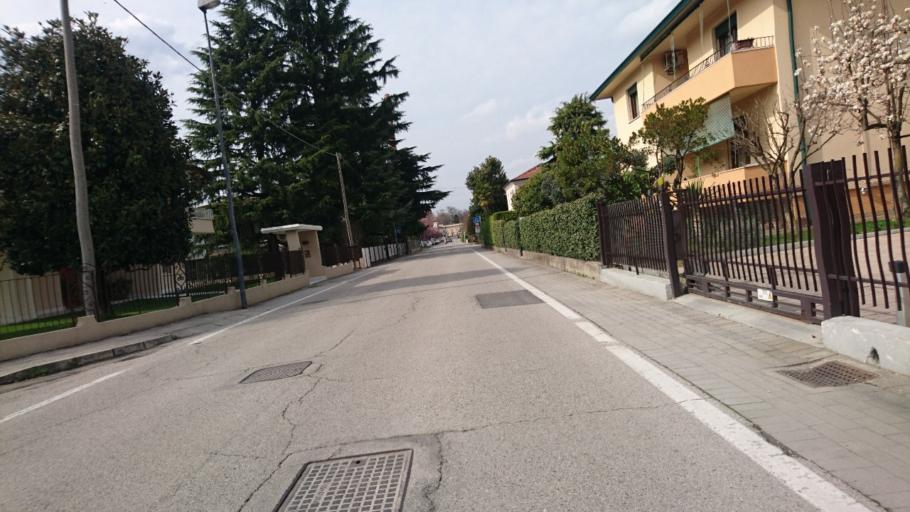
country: IT
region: Veneto
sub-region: Provincia di Padova
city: Piazzola sul Brenta
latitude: 45.5403
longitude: 11.7896
